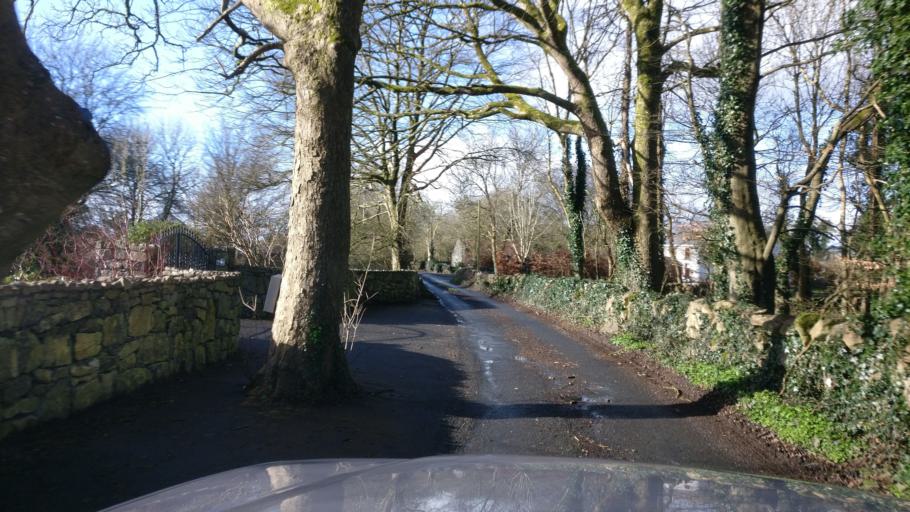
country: IE
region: Connaught
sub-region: County Galway
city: Athenry
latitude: 53.2293
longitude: -8.7471
